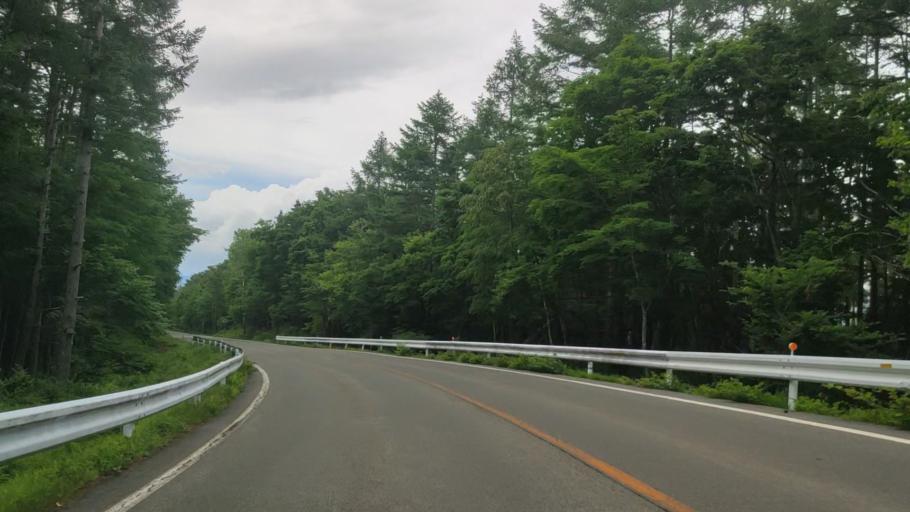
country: JP
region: Yamanashi
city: Fujikawaguchiko
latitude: 35.4265
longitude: 138.7398
